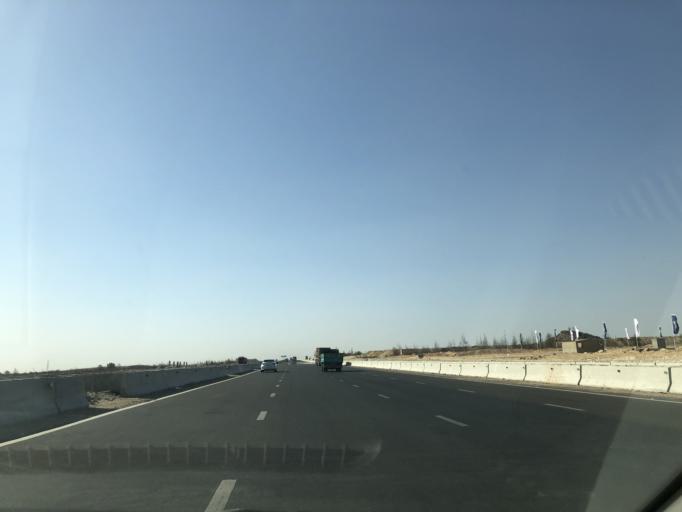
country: EG
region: Al Jizah
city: Madinat Sittah Uktubar
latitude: 29.9792
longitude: 30.8659
